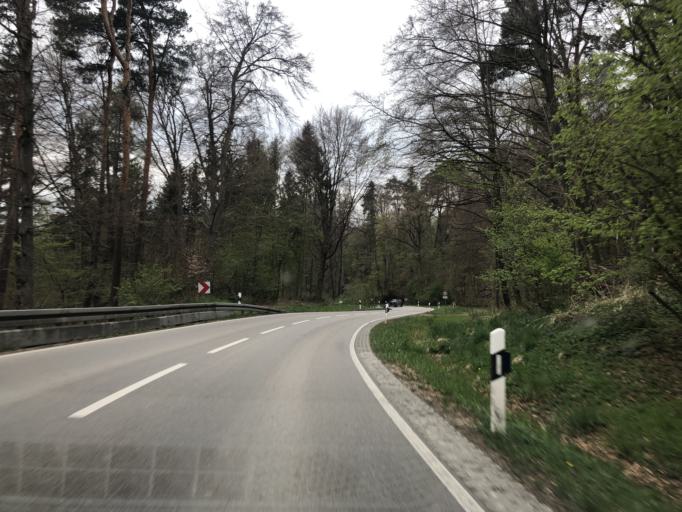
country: DE
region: Bavaria
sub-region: Upper Bavaria
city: Kirchdorf
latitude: 48.4425
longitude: 11.6747
